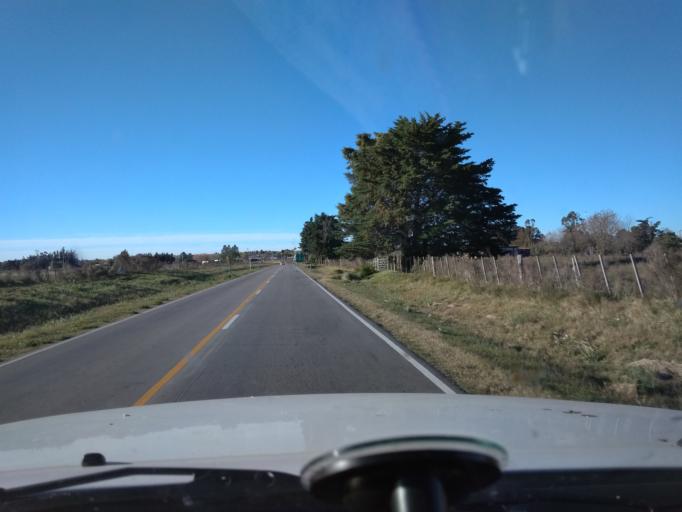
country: UY
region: Canelones
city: Santa Rosa
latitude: -34.5083
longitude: -56.0520
